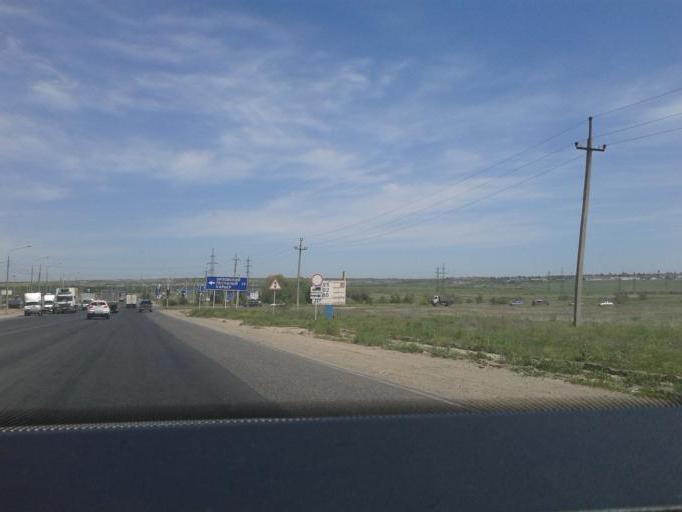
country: RU
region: Volgograd
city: Vodstroy
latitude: 48.8188
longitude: 44.5253
